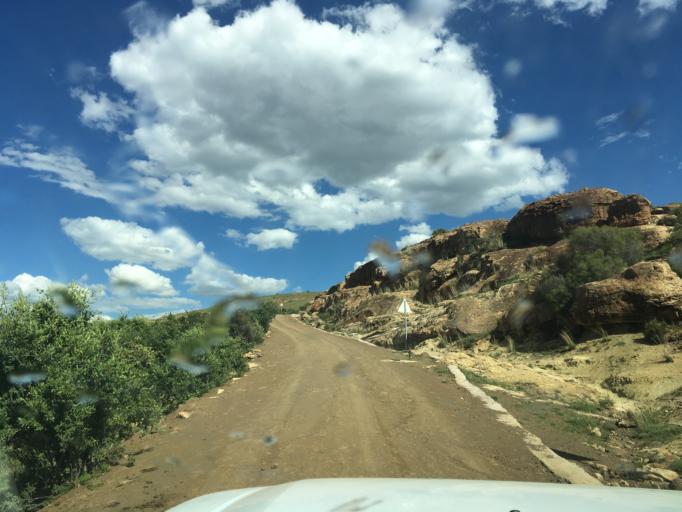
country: LS
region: Quthing
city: Quthing
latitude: -30.2319
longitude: 27.9665
